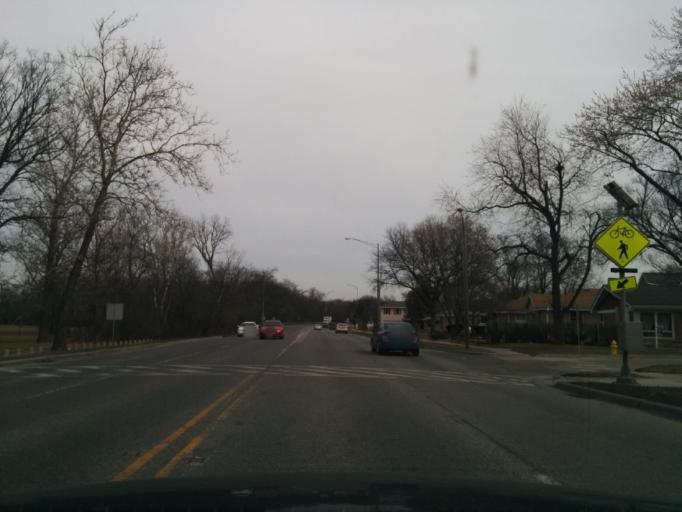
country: US
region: Illinois
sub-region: Cook County
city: Western Springs
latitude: 41.8203
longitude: -87.9033
